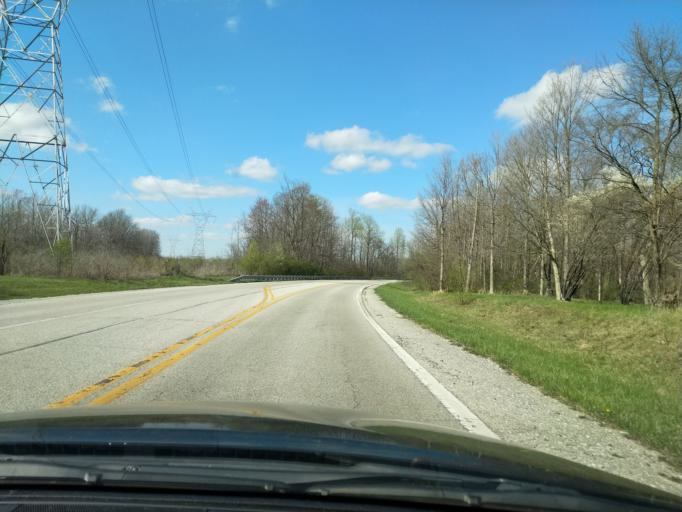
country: US
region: Indiana
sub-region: Marion County
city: Meridian Hills
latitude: 39.8831
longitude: -86.2311
